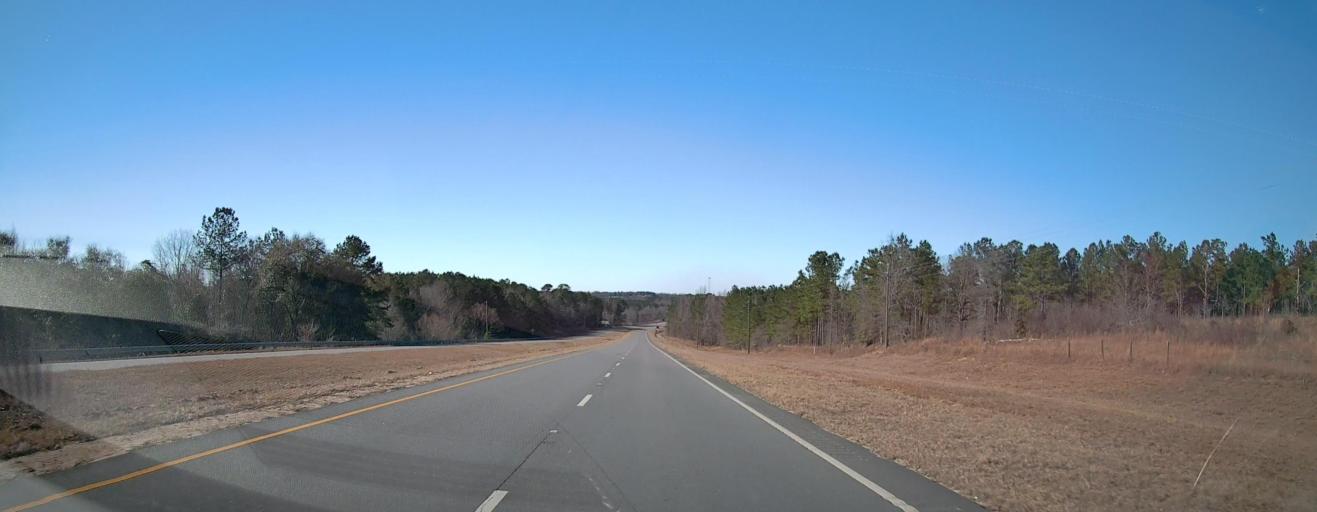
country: US
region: Georgia
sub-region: Taylor County
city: Butler
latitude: 32.6130
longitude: -84.2397
